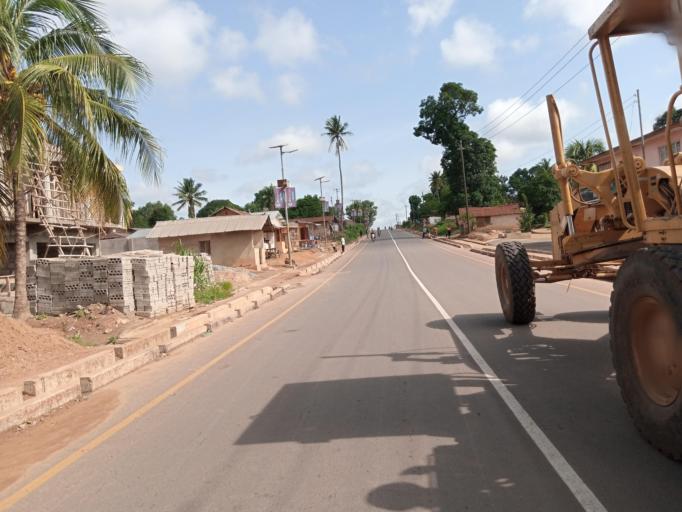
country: SL
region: Southern Province
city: Bo
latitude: 7.9519
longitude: -11.7178
